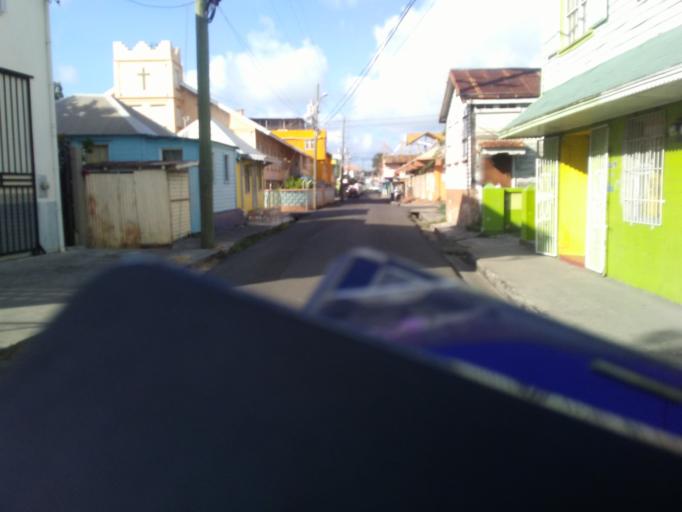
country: AG
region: Saint John
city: Saint John's
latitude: 17.1241
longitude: -61.8447
